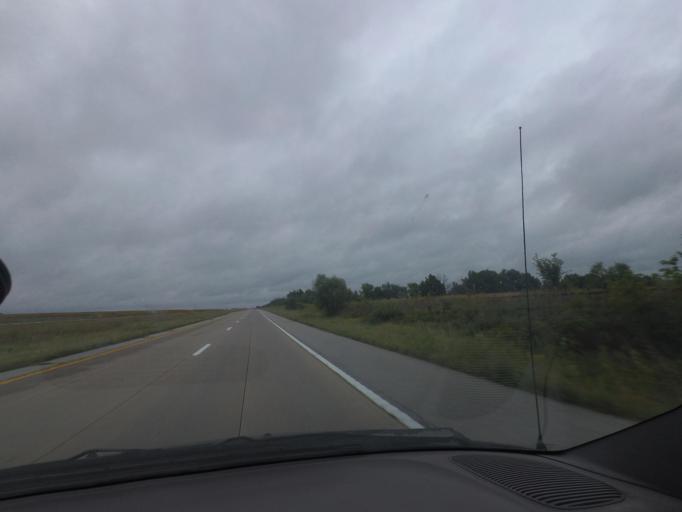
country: US
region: Missouri
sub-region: Marion County
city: Monroe City
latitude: 39.6633
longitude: -91.8394
